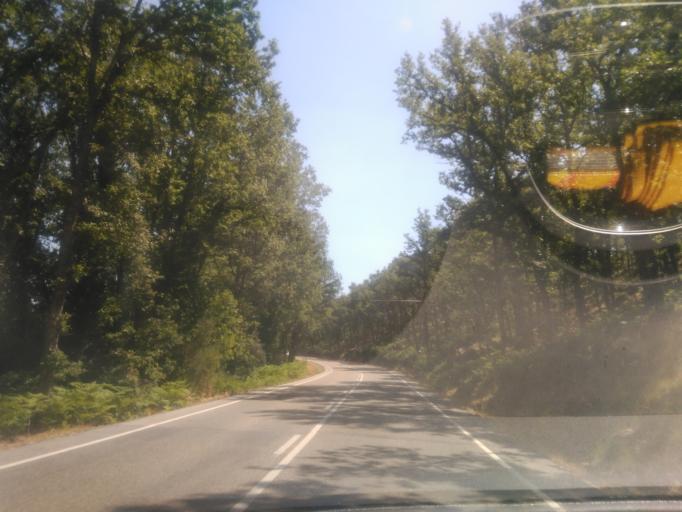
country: ES
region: Castille and Leon
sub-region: Provincia de Zamora
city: Galende
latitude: 42.1184
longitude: -6.6954
